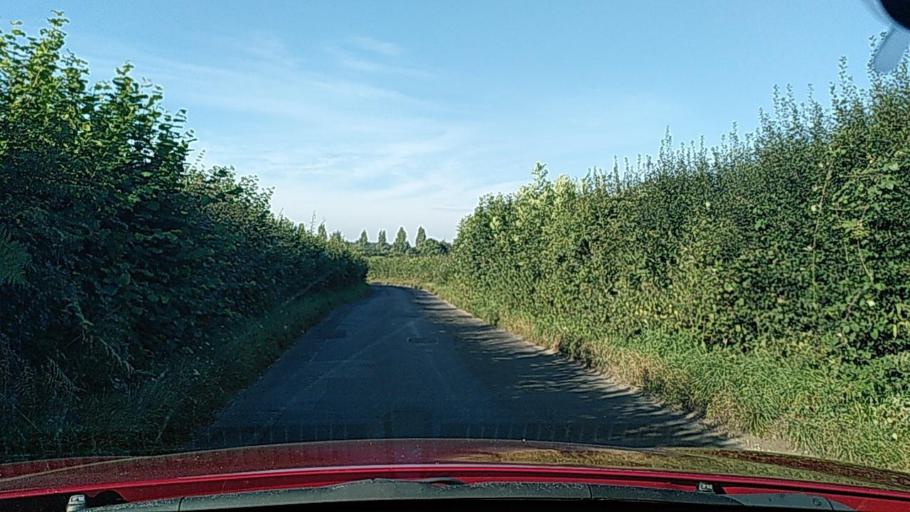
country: GB
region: England
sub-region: Oxfordshire
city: Sonning Common
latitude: 51.4947
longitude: -0.9507
